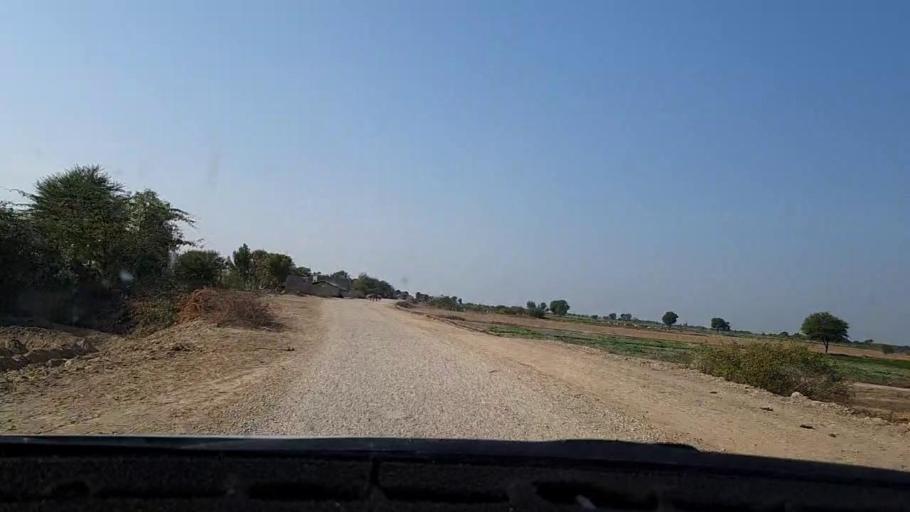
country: PK
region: Sindh
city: Tando Mittha Khan
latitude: 25.8150
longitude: 69.3072
